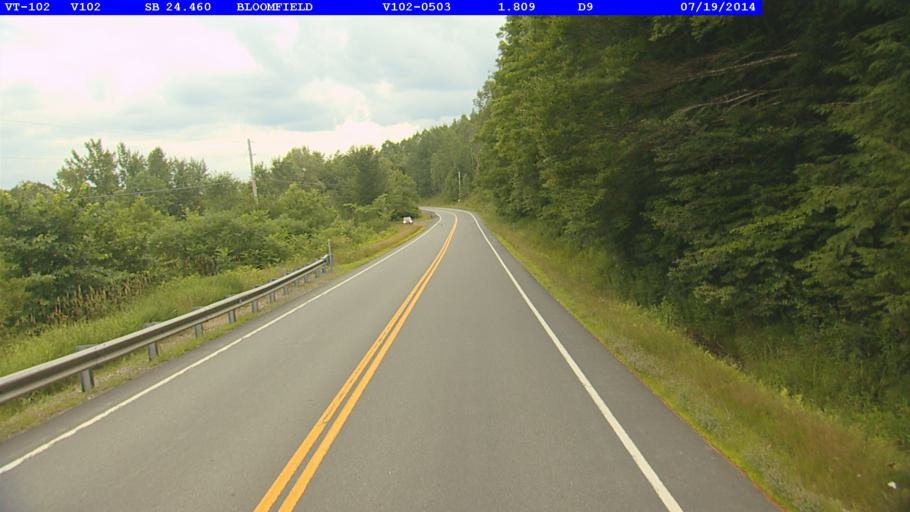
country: US
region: New Hampshire
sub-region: Coos County
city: Stratford
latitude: 44.7668
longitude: -71.6097
